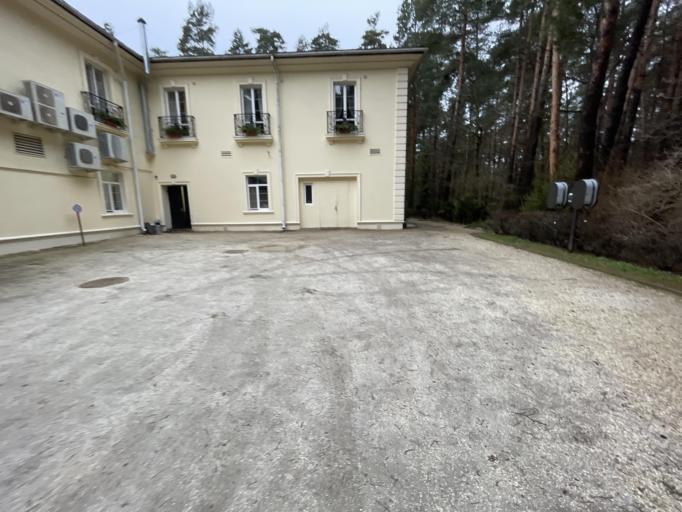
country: BY
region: Grodnenskaya
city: Hrodna
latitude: 53.6807
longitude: 23.7877
